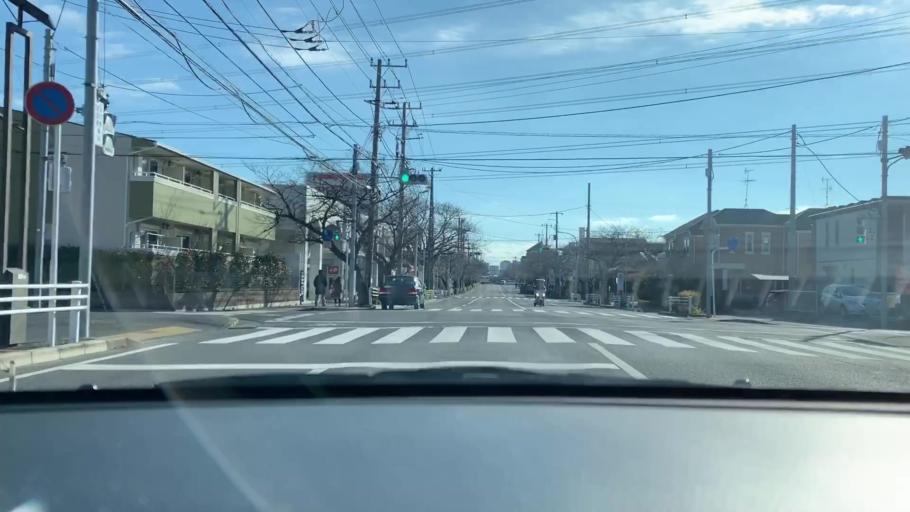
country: JP
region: Tokyo
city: Urayasu
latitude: 35.6547
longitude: 139.8957
